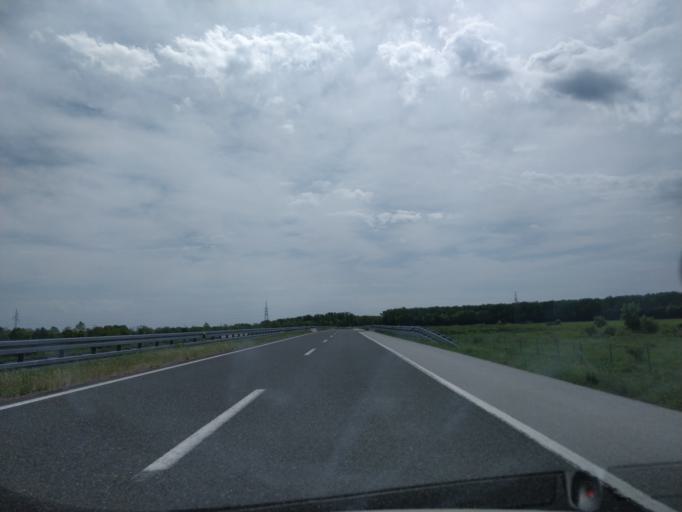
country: HR
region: Zagrebacka
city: Mraclin
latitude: 45.6488
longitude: 16.0842
